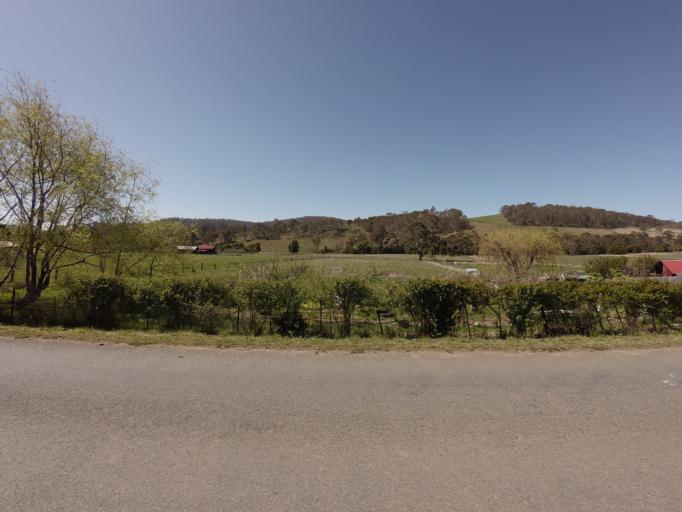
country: AU
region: Tasmania
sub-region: Derwent Valley
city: New Norfolk
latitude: -42.6195
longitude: 146.7172
